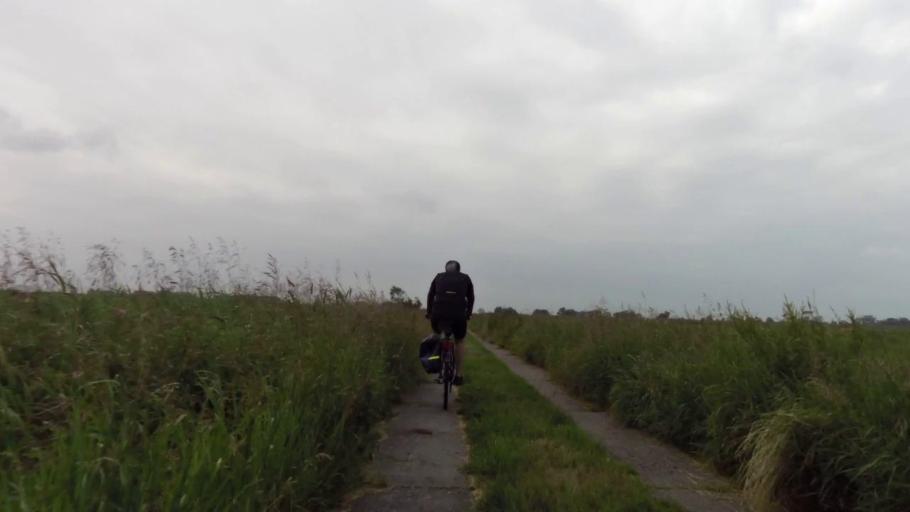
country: PL
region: West Pomeranian Voivodeship
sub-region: Powiat goleniowski
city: Stepnica
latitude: 53.5607
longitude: 14.6997
